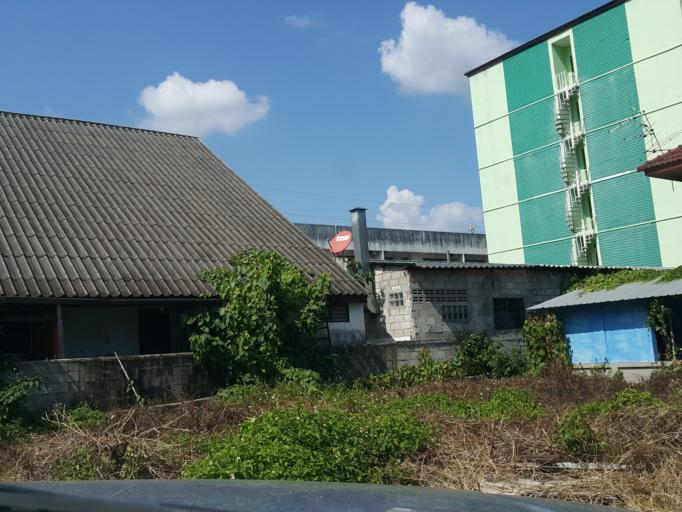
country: TH
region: Chiang Mai
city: Chiang Mai
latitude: 18.7929
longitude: 99.0284
